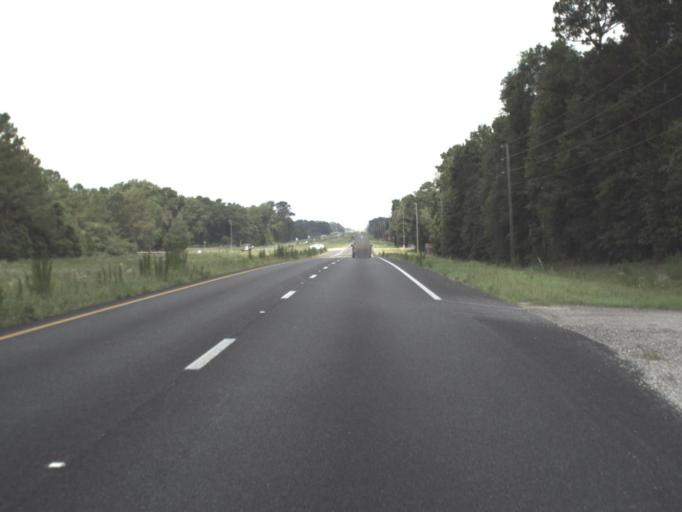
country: US
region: Florida
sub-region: Levy County
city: Williston
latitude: 29.4027
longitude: -82.5123
